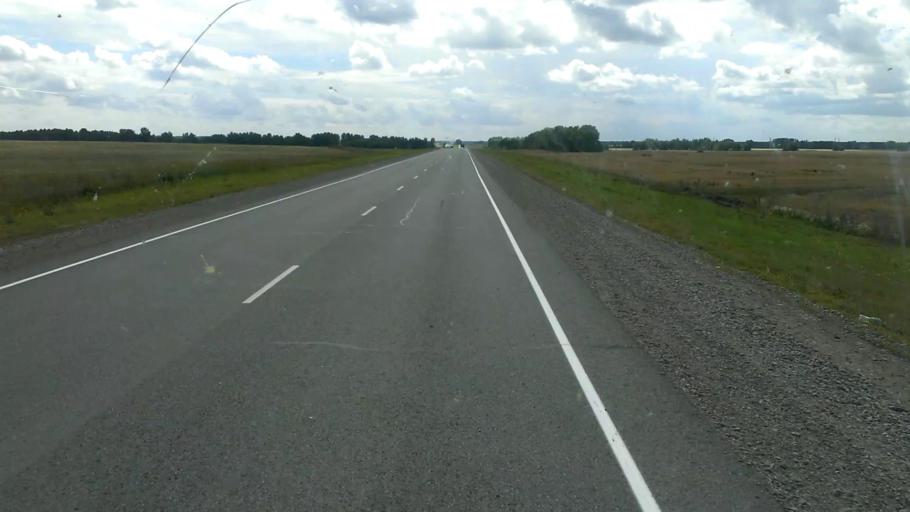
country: RU
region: Altai Krai
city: Troitskoye
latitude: 52.8979
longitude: 84.8336
